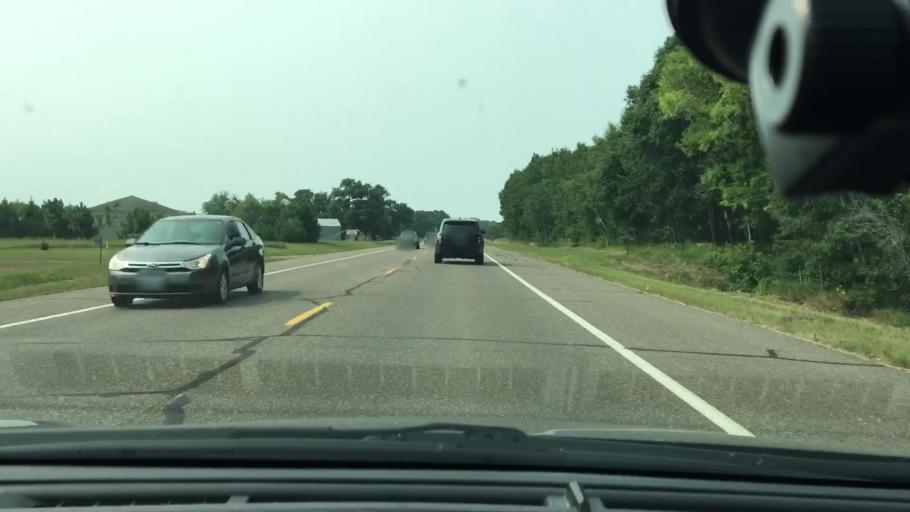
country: US
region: Minnesota
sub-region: Crow Wing County
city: Breezy Point
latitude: 46.4914
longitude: -94.1523
